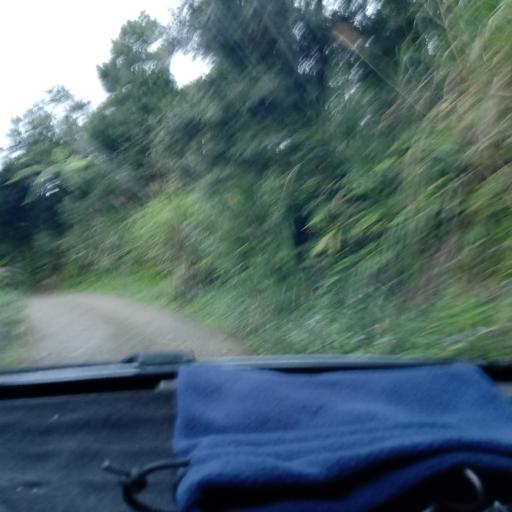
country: TW
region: Taiwan
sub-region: Yilan
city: Yilan
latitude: 24.8122
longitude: 121.6916
